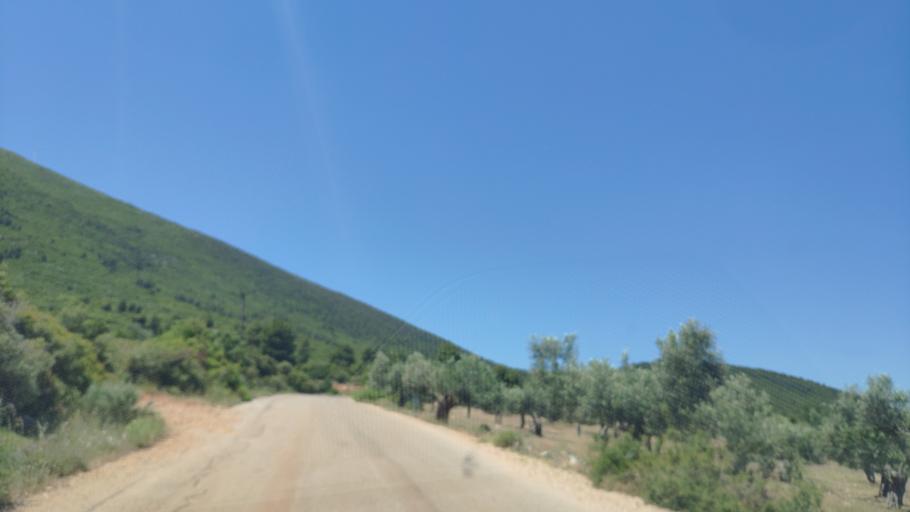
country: GR
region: Central Greece
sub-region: Nomos Voiotias
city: Kaparellion
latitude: 38.2103
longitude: 23.1861
